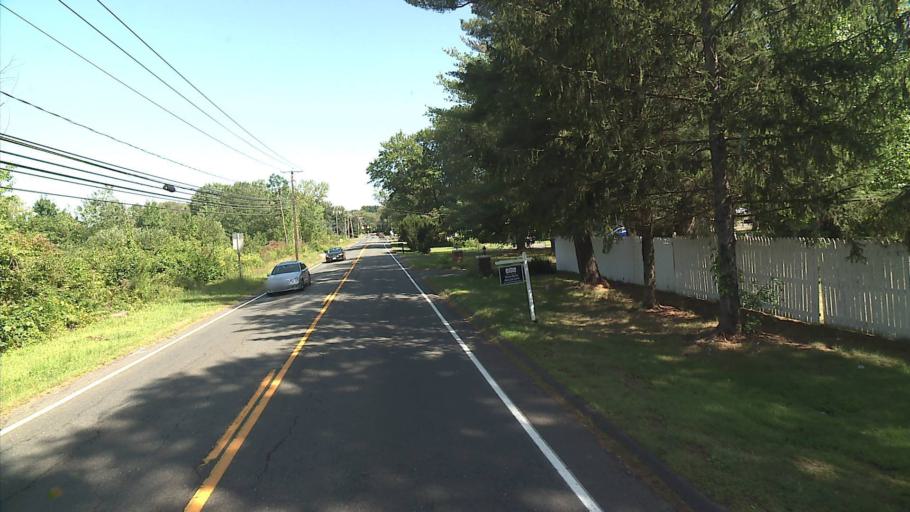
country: US
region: Connecticut
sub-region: Hartford County
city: Blue Hills
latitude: 41.8307
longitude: -72.7515
